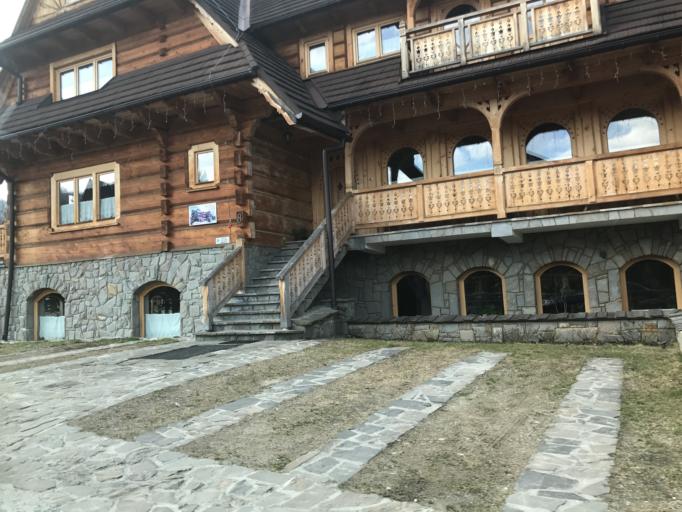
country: PL
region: Lesser Poland Voivodeship
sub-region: Powiat tatrzanski
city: Zakopane
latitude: 49.2839
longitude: 19.9461
